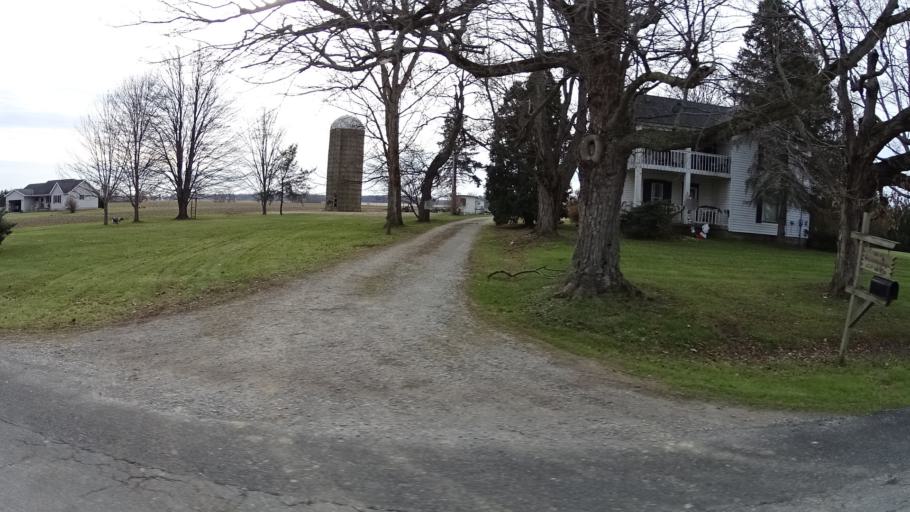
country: US
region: Ohio
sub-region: Lorain County
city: Lagrange
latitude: 41.1366
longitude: -82.1044
